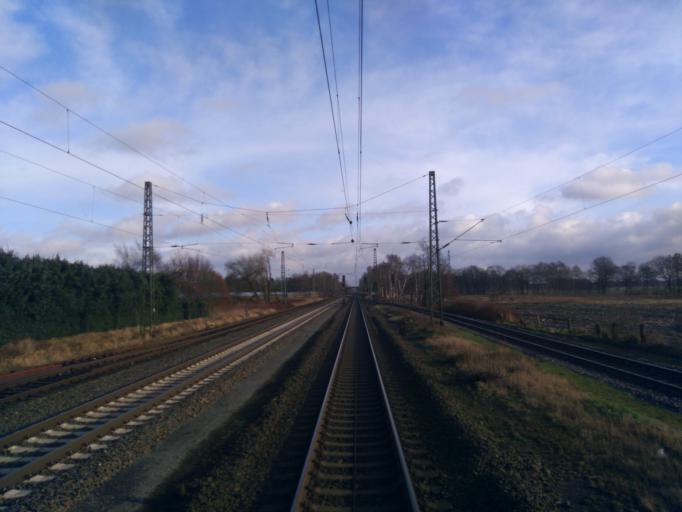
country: DE
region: Lower Saxony
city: Hassendorf
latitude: 53.1014
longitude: 9.2576
